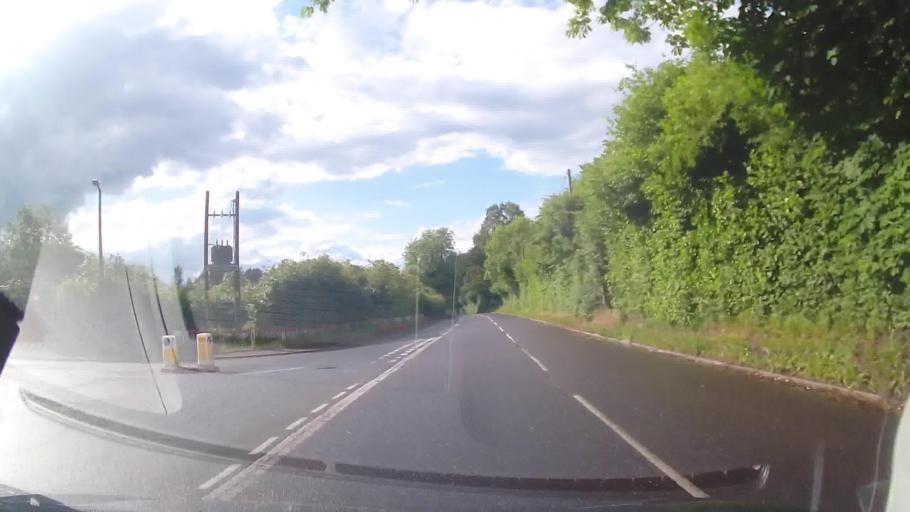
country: GB
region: England
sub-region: Telford and Wrekin
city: Ironbridge
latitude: 52.6334
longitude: -2.5053
